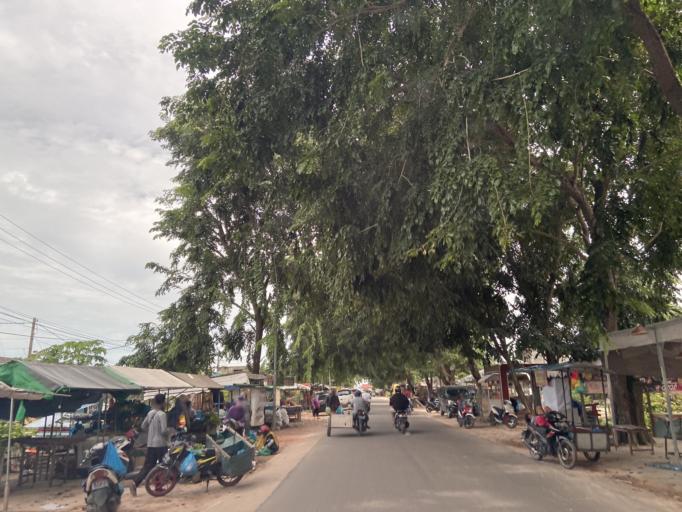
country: SG
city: Singapore
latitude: 1.0355
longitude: 103.9765
